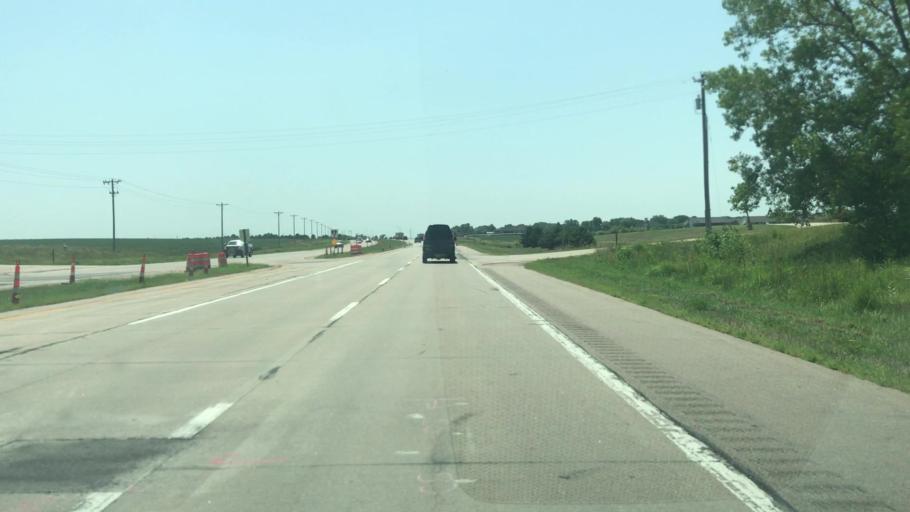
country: US
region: Nebraska
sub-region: Adams County
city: Hastings
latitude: 40.6483
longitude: -98.3826
